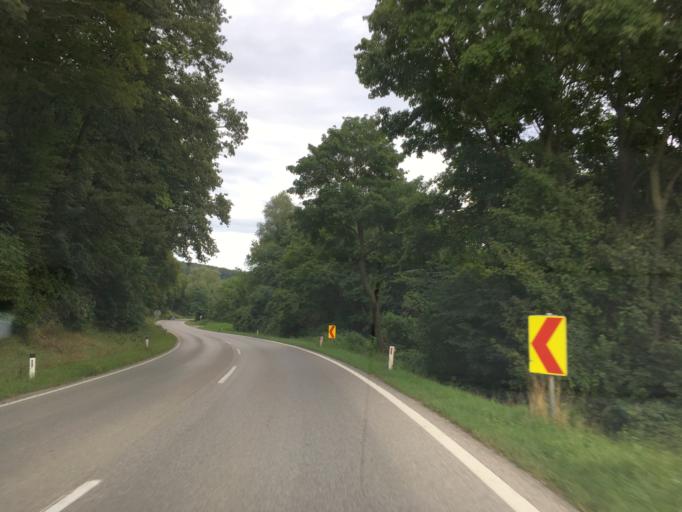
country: AT
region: Lower Austria
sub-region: Politischer Bezirk Tulln
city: Wordern
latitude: 48.3171
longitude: 16.2256
